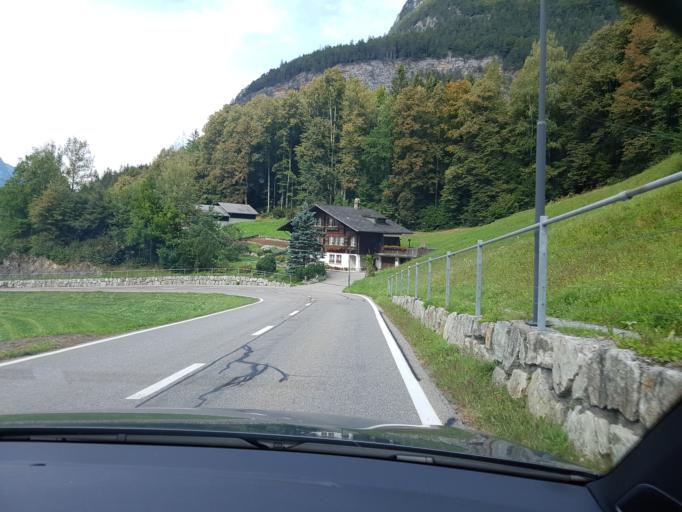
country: CH
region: Bern
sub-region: Interlaken-Oberhasli District
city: Meiringen
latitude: 46.7083
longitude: 8.2400
